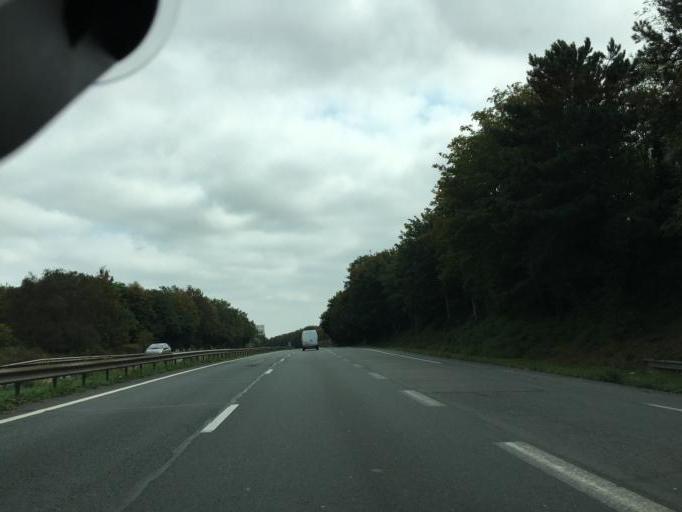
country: FR
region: Nord-Pas-de-Calais
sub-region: Departement du Pas-de-Calais
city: Noyelles-Godault
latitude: 50.4270
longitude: 3.0013
